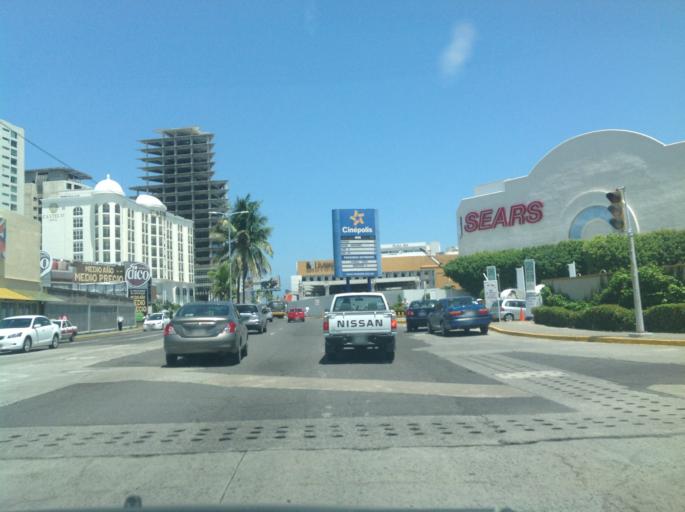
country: MX
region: Veracruz
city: Boca del Rio
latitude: 19.1404
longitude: -96.1079
